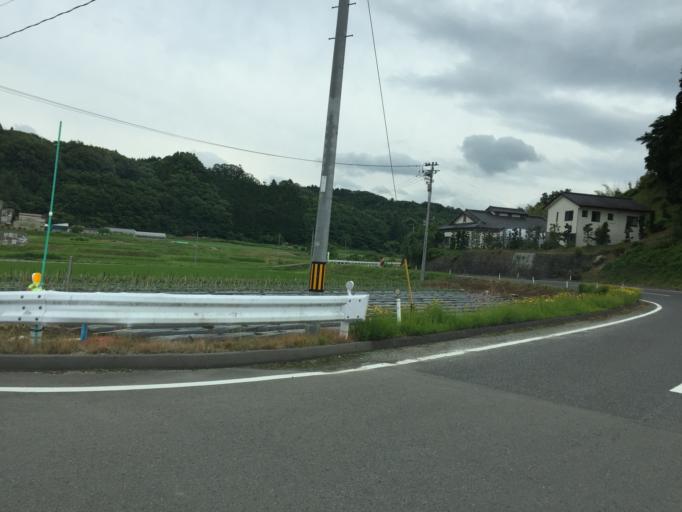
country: JP
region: Fukushima
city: Funehikimachi-funehiki
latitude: 37.4182
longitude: 140.6529
